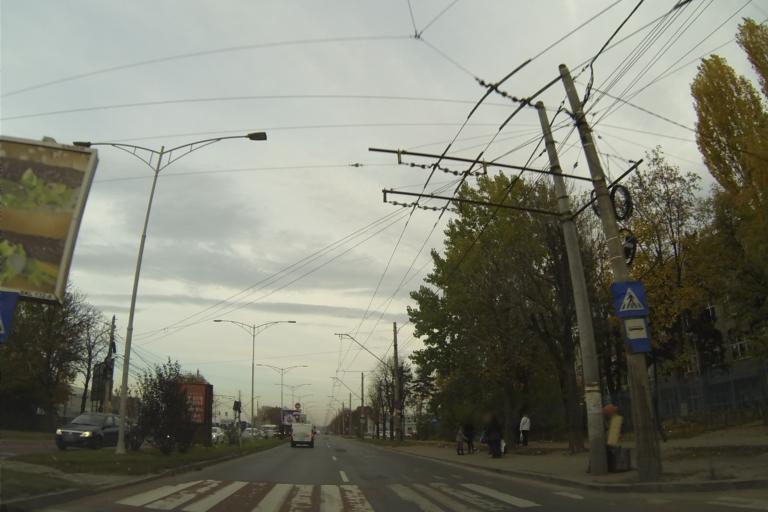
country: RO
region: Ilfov
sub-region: Comuna Chiajna
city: Chiajna
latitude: 44.4355
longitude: 25.9759
